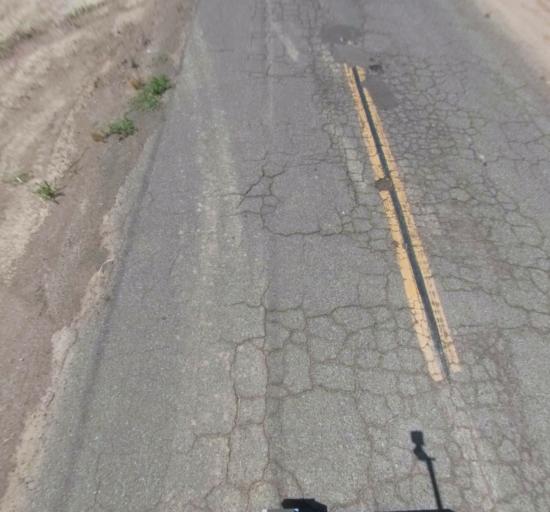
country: US
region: California
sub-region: Madera County
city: Chowchilla
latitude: 37.0770
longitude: -120.3469
